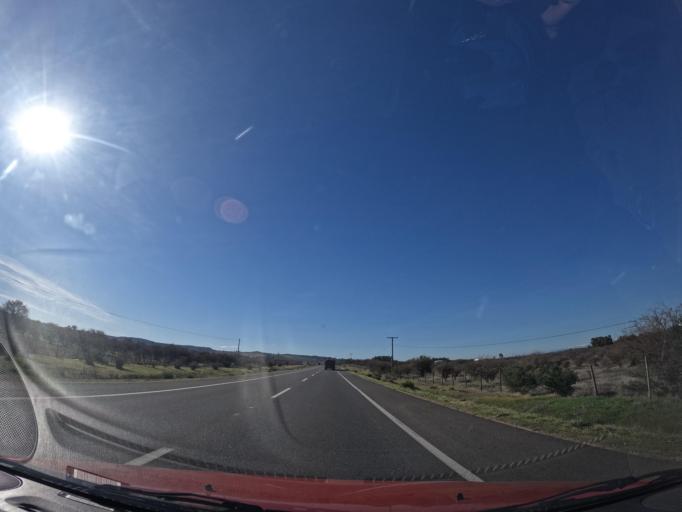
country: CL
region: Maule
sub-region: Provincia de Cauquenes
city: Cauquenes
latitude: -35.9537
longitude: -72.2099
